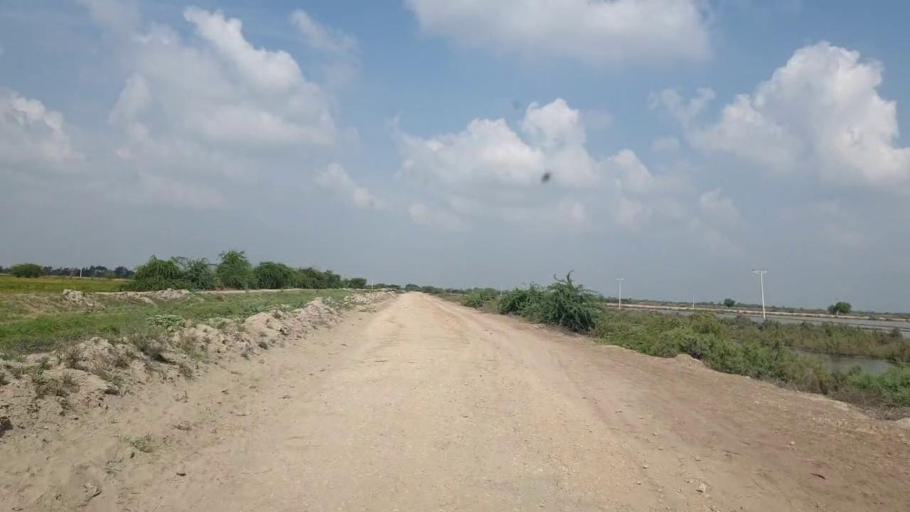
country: PK
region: Sindh
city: Badin
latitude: 24.5040
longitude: 68.6557
